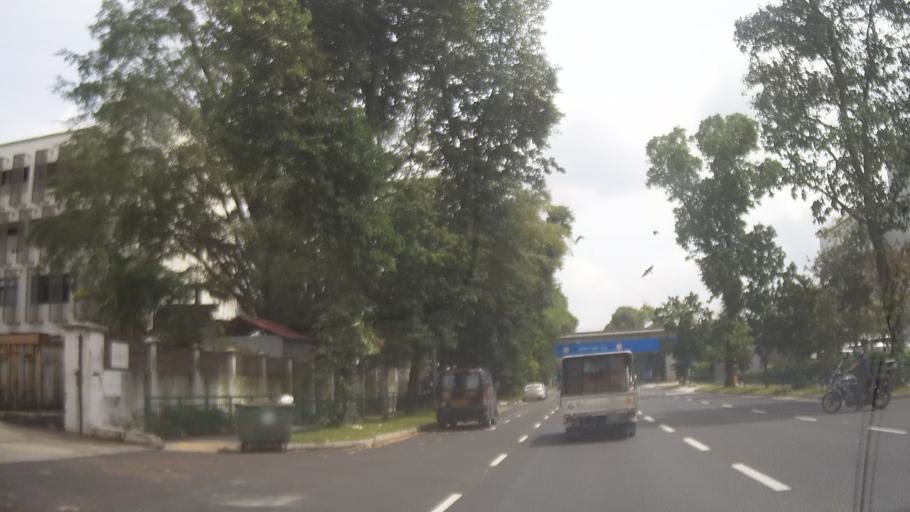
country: MY
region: Johor
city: Johor Bahru
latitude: 1.4166
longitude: 103.7468
